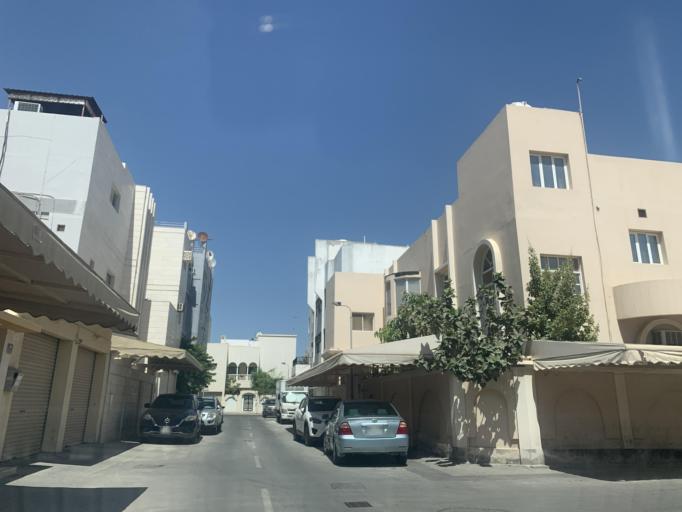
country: BH
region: Manama
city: Jidd Hafs
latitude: 26.2118
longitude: 50.5623
